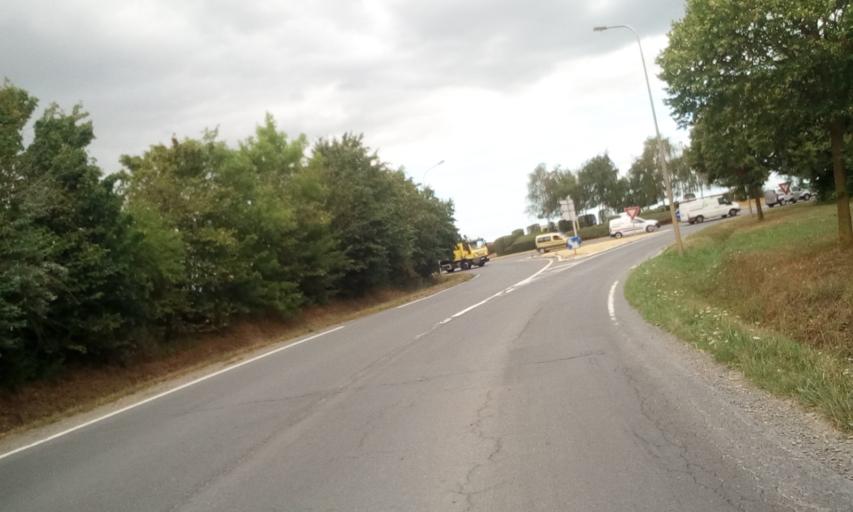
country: FR
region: Lower Normandy
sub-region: Departement du Calvados
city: Bellengreville
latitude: 49.1283
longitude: -0.2180
